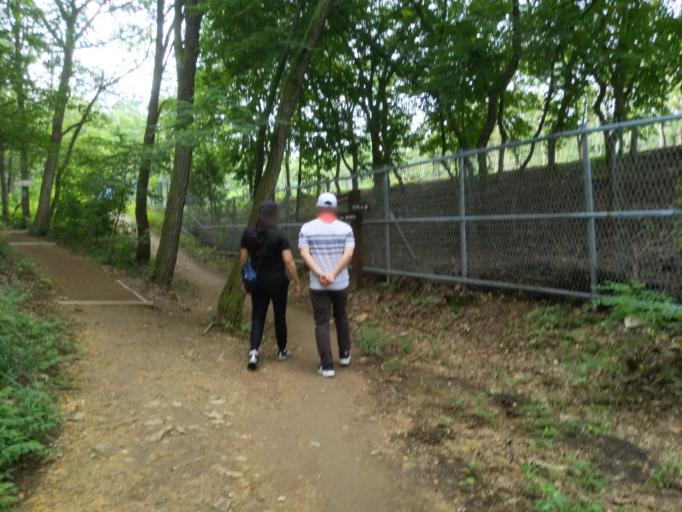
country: KR
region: Daegu
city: Hwawon
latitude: 35.7947
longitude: 128.5261
